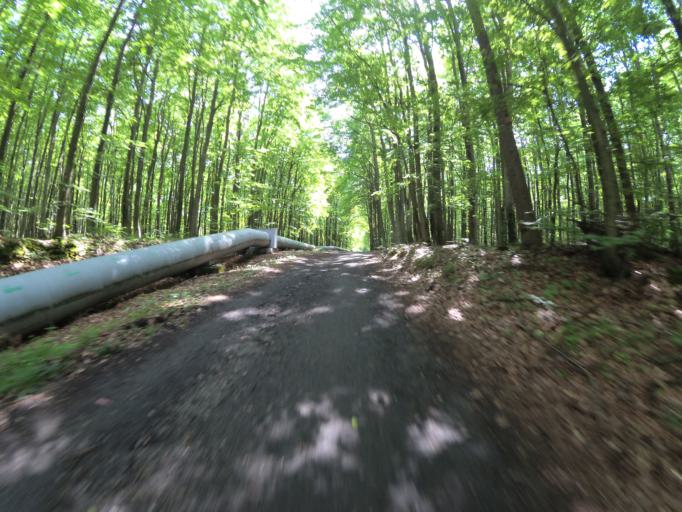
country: PL
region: Pomeranian Voivodeship
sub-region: Gdynia
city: Wielki Kack
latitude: 54.5044
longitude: 18.4926
